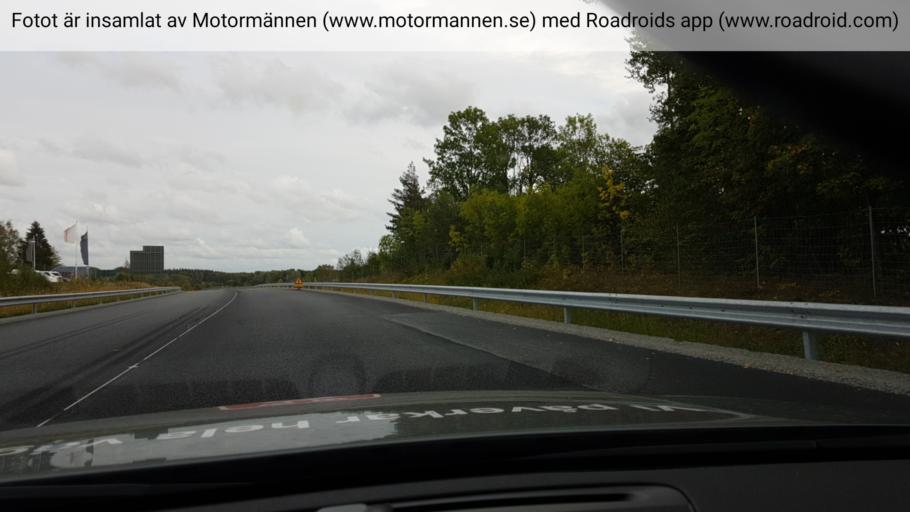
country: SE
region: Stockholm
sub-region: Norrtalje Kommun
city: Norrtalje
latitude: 59.7405
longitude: 18.6964
